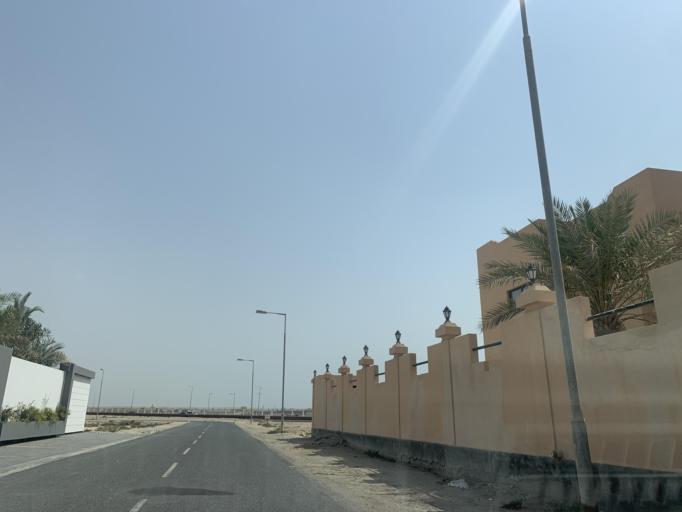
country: BH
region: Central Governorate
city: Madinat Hamad
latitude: 26.1616
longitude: 50.4755
